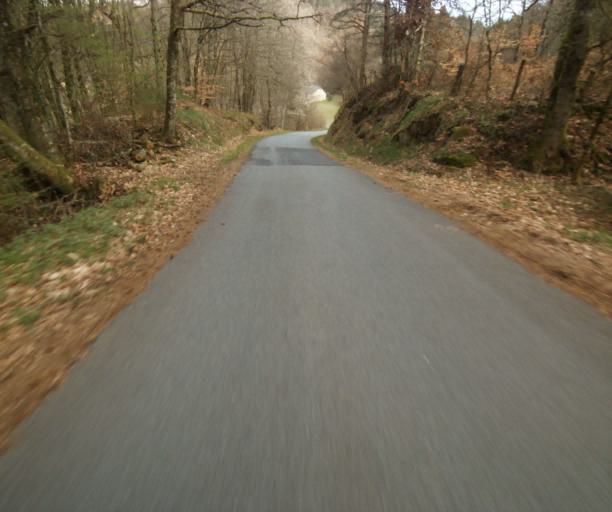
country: FR
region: Limousin
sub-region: Departement de la Correze
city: Correze
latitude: 45.4182
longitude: 1.8983
